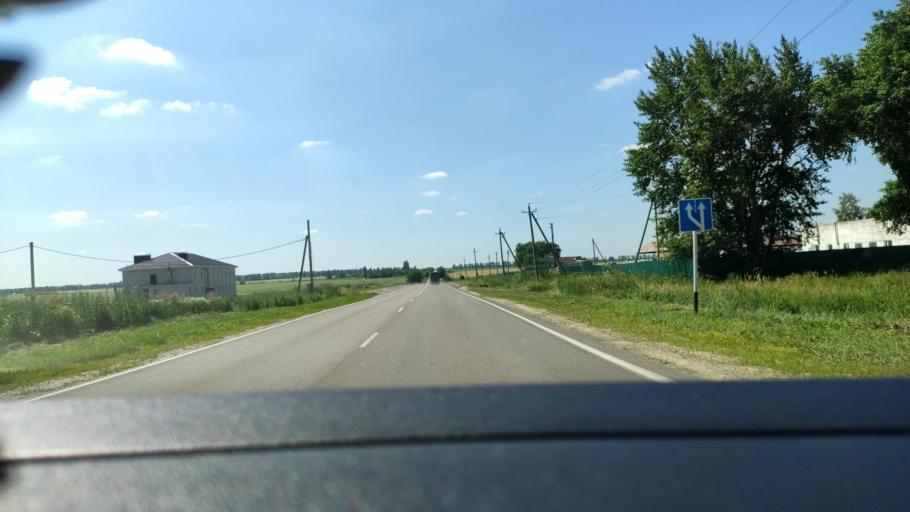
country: RU
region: Voronezj
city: Novaya Usman'
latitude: 51.5824
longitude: 39.3746
